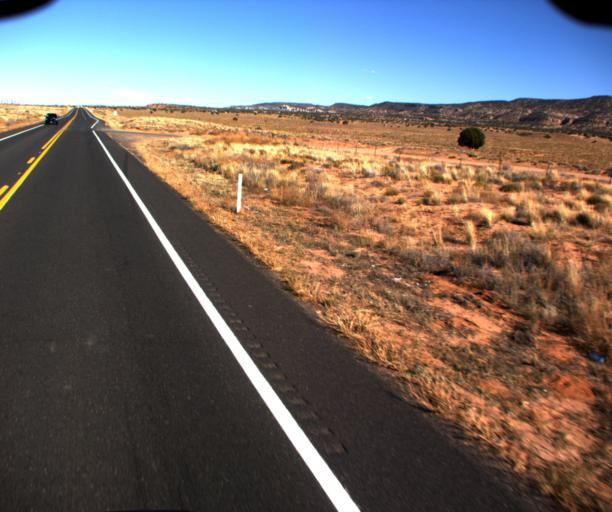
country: US
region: Arizona
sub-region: Coconino County
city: Kaibito
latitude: 36.3970
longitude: -110.8649
